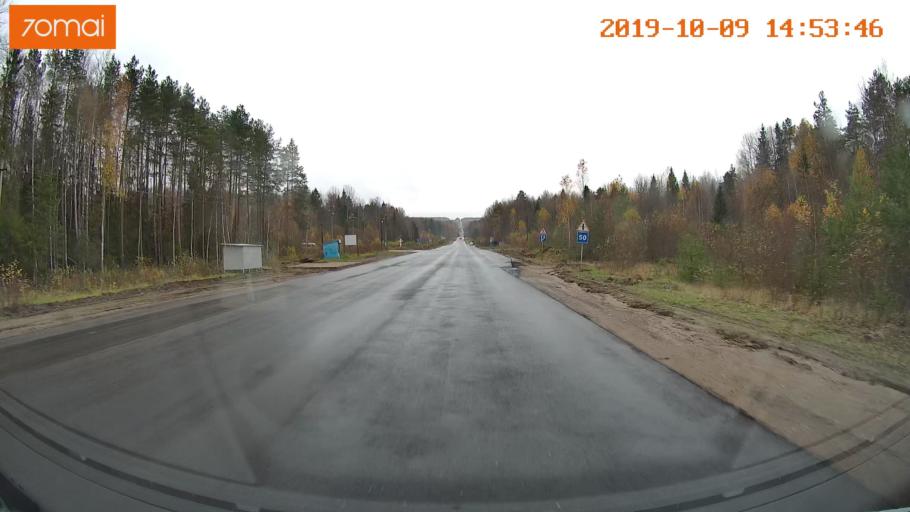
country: RU
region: Kostroma
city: Chistyye Bory
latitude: 58.3637
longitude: 41.6399
